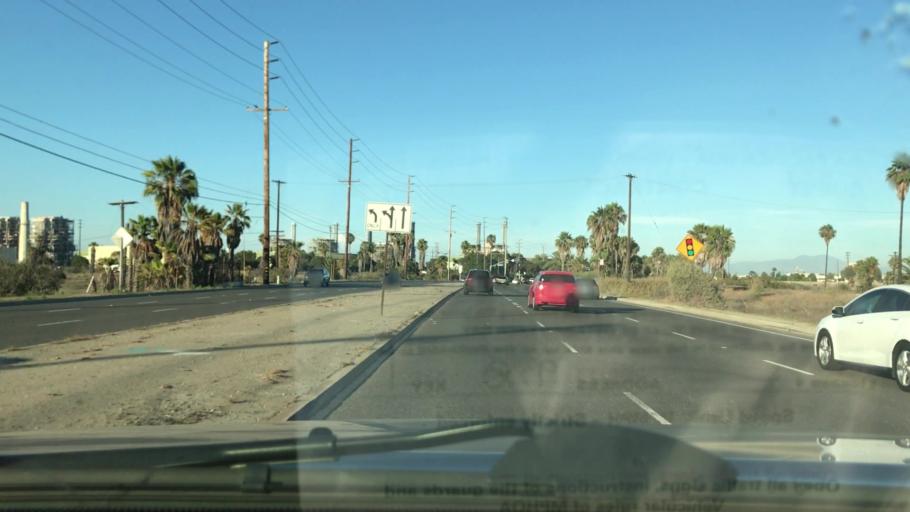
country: US
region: California
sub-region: Orange County
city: Seal Beach
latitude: 33.7591
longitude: -118.1070
